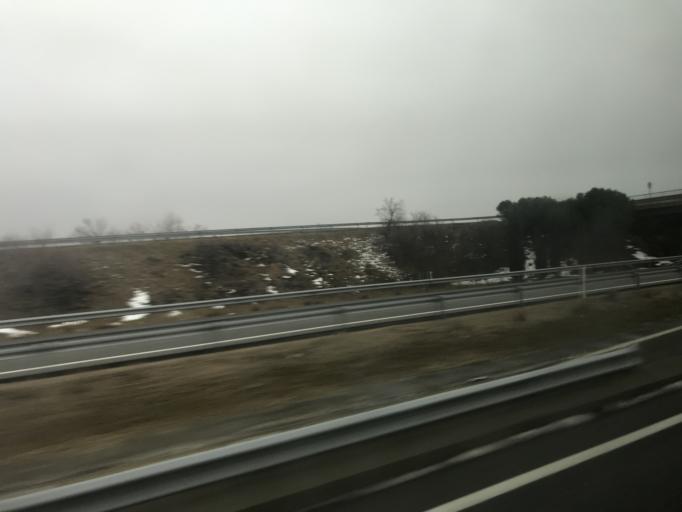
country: ES
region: Castille and Leon
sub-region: Provincia de Burgos
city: Villazopeque
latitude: 42.2035
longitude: -4.0179
